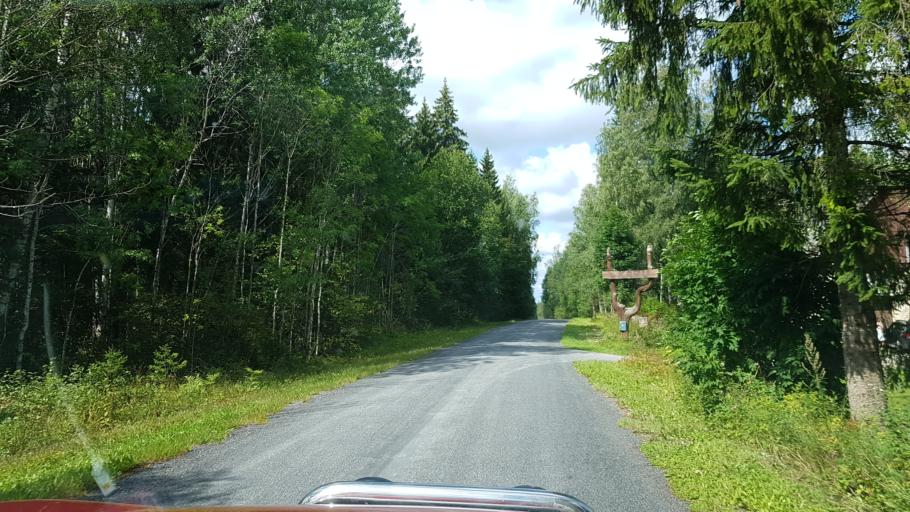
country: EE
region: Raplamaa
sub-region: Rapla vald
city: Rapla
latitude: 58.9537
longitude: 24.6654
